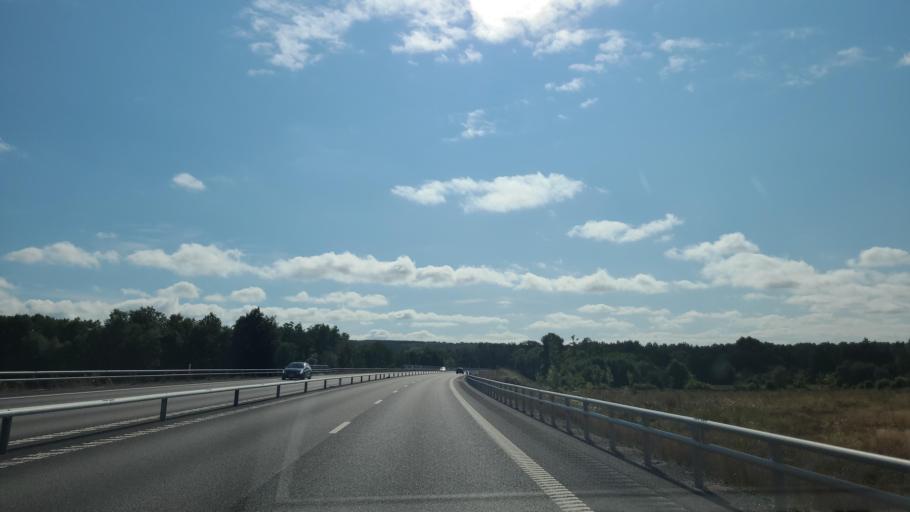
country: SE
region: Skane
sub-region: Kristianstads Kommun
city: Onnestad
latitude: 55.9531
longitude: 13.9186
